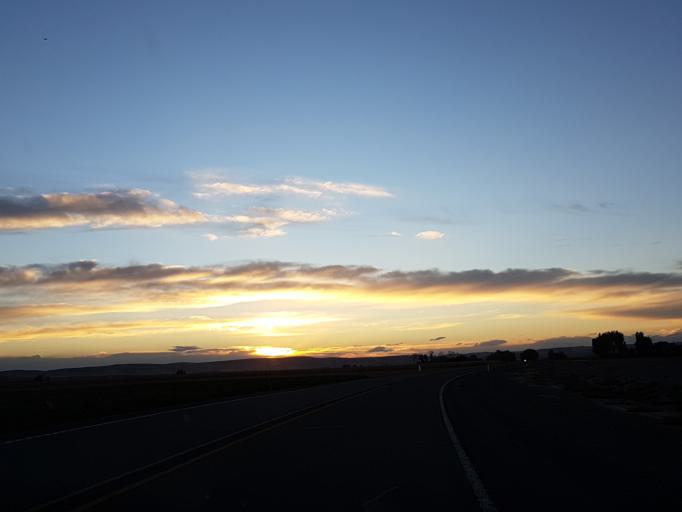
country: US
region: Oregon
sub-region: Malheur County
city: Vale
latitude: 43.9361
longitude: -117.3177
